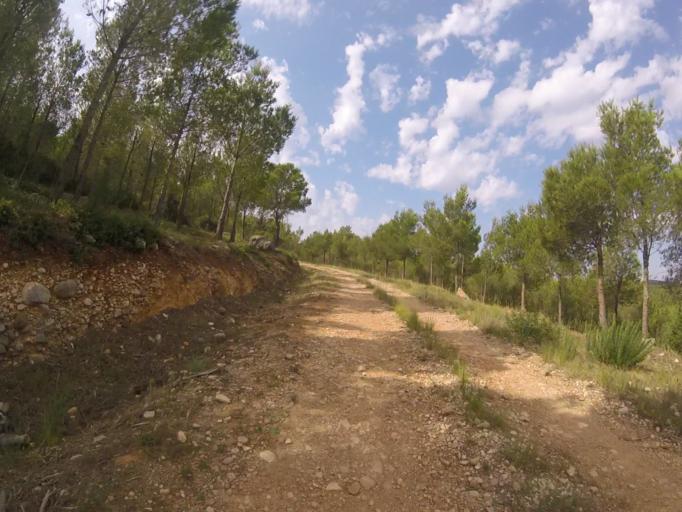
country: ES
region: Valencia
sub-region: Provincia de Castello
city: Alcala de Xivert
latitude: 40.3642
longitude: 0.2029
